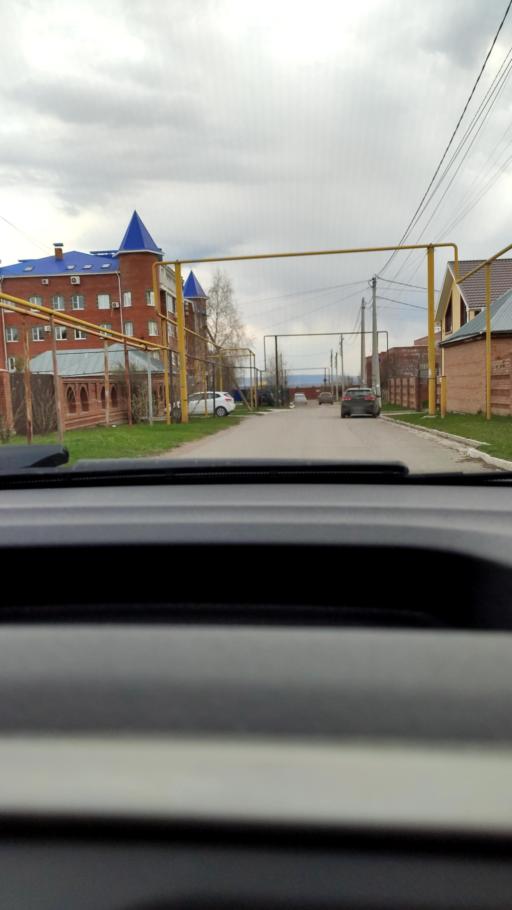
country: RU
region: Samara
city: Podstepki
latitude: 53.5092
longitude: 49.2380
